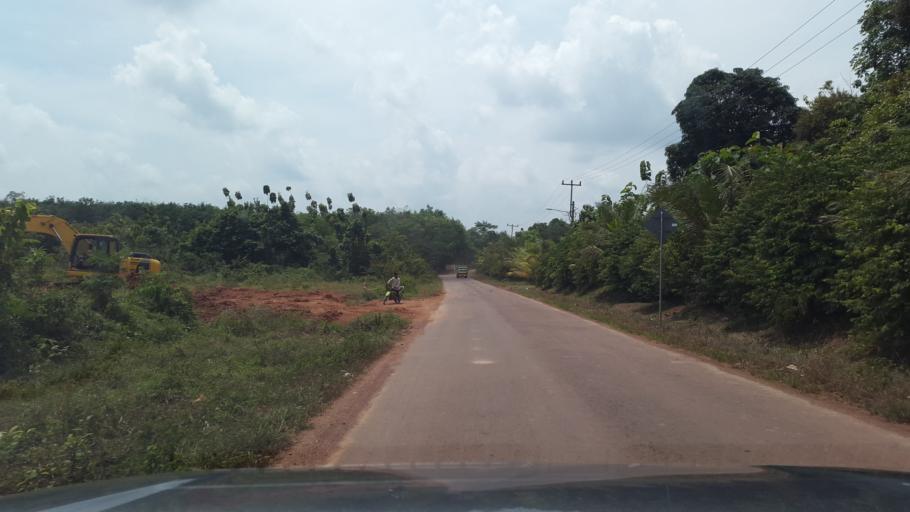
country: ID
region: South Sumatra
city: Sungaigerong
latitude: -3.1622
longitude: 104.8939
